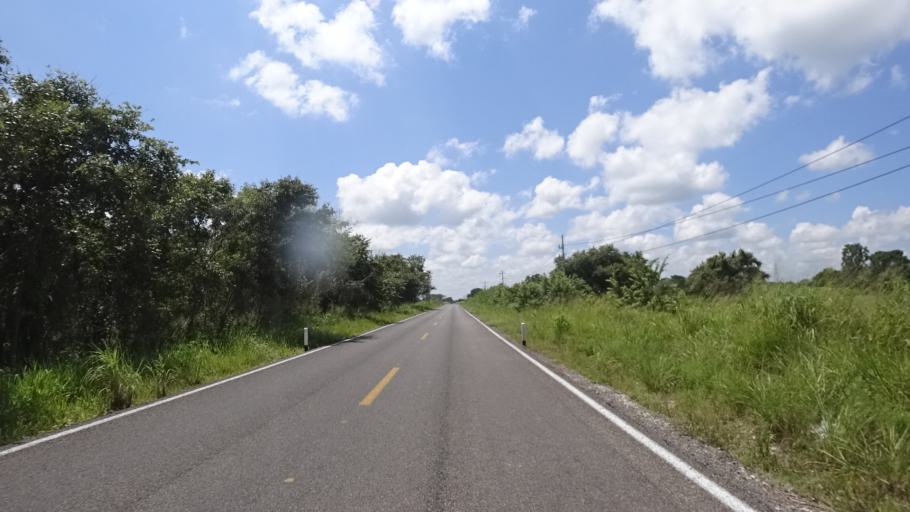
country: MX
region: Campeche
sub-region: Carmen
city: Licenciado Gustavo Diaz Ordaz (18 de Marzo)
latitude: 18.6455
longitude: -90.9811
